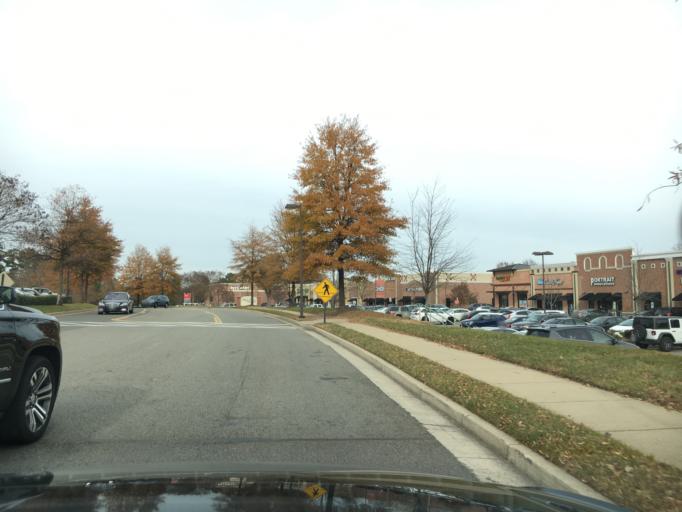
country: US
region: Virginia
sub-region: Henrico County
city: Short Pump
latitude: 37.6547
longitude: -77.6152
